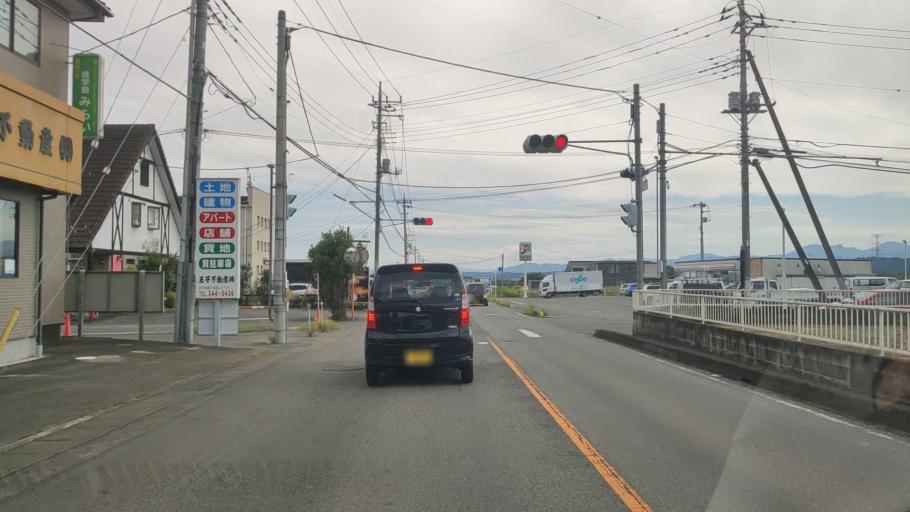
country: JP
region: Gunma
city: Kanekomachi
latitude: 36.3738
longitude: 138.9721
